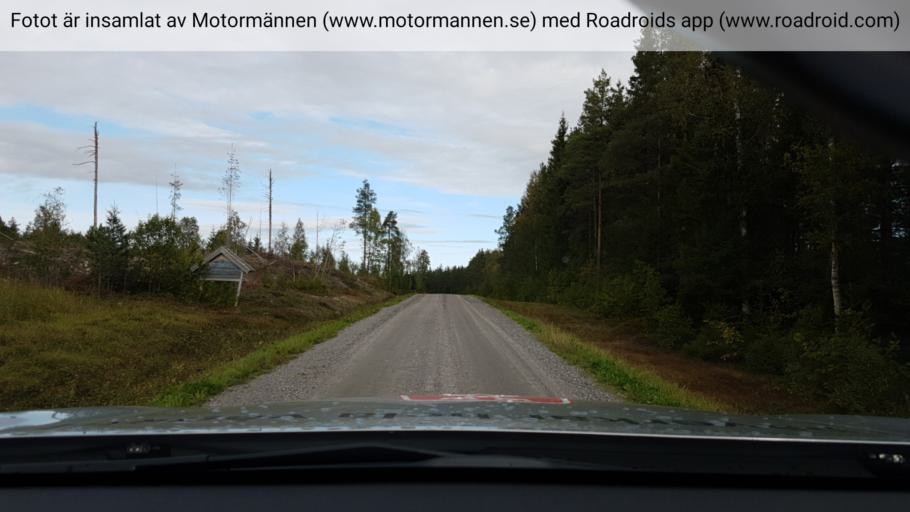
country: SE
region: Vaesterbotten
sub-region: Skelleftea Kommun
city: Byske
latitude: 65.1246
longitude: 21.2046
